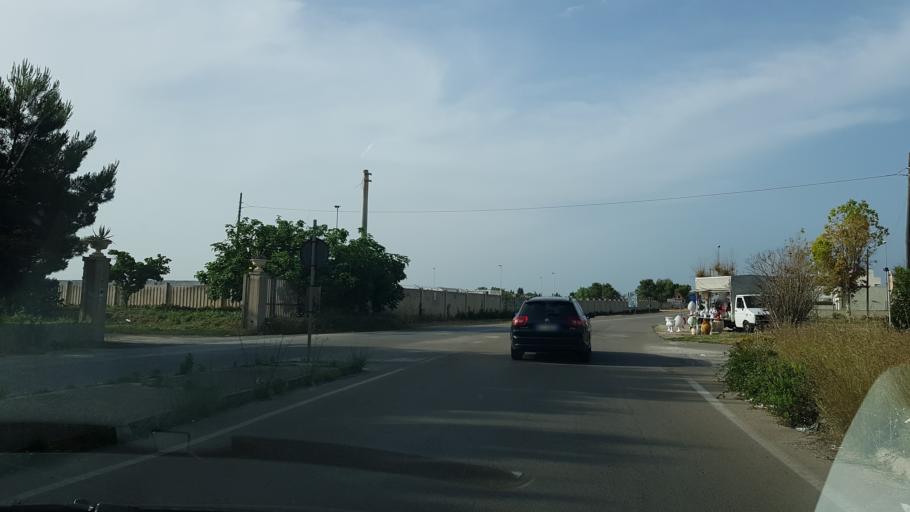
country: IT
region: Apulia
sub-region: Provincia di Lecce
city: Porto Cesareo
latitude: 40.2958
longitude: 17.8557
